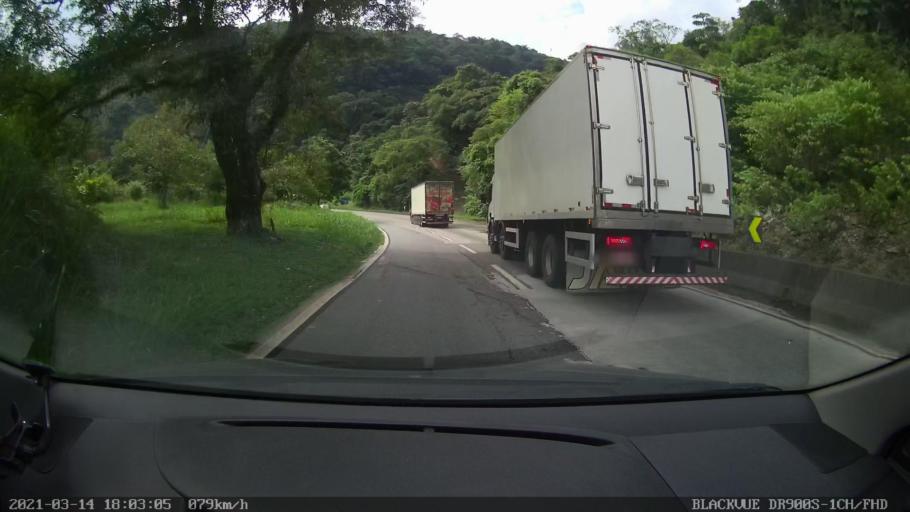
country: BR
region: Rio de Janeiro
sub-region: Petropolis
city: Petropolis
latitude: -22.5484
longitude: -43.2366
